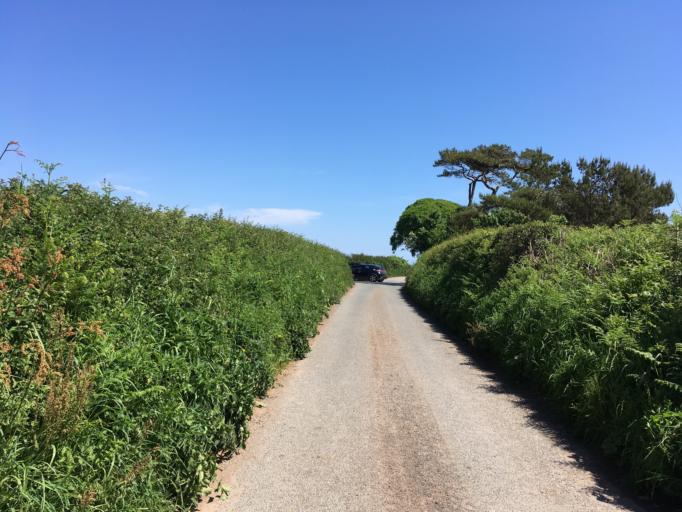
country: GB
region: England
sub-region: Devon
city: Dartmouth
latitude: 50.3510
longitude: -3.5382
